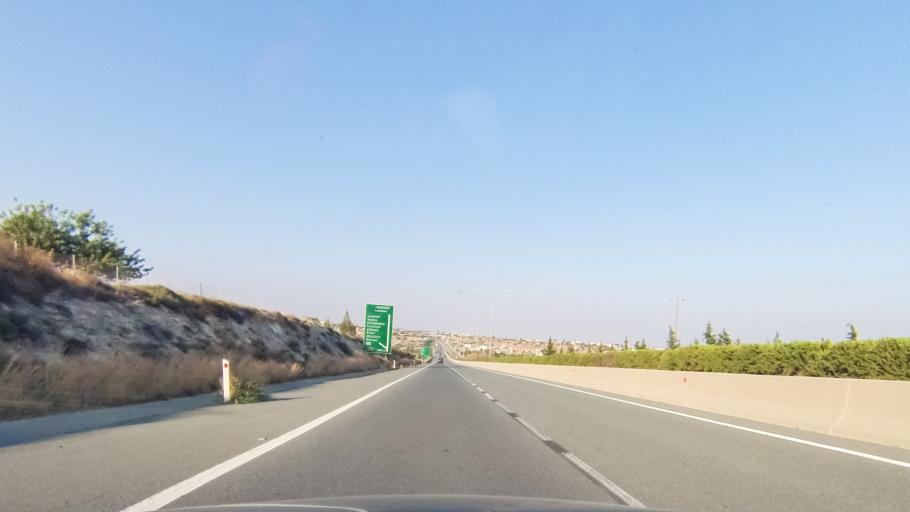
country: CY
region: Limassol
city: Erimi
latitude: 34.6823
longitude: 32.8995
